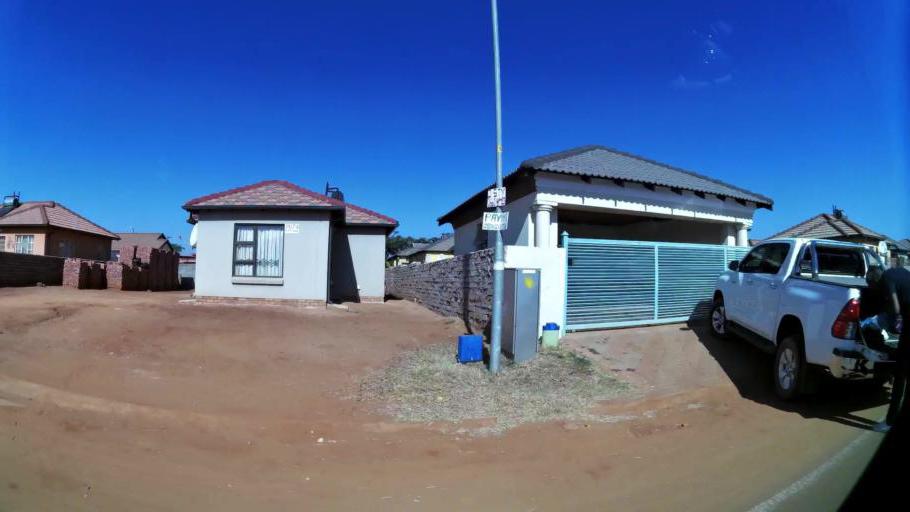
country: ZA
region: North-West
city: Ga-Rankuwa
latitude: -25.6336
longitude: 28.0773
